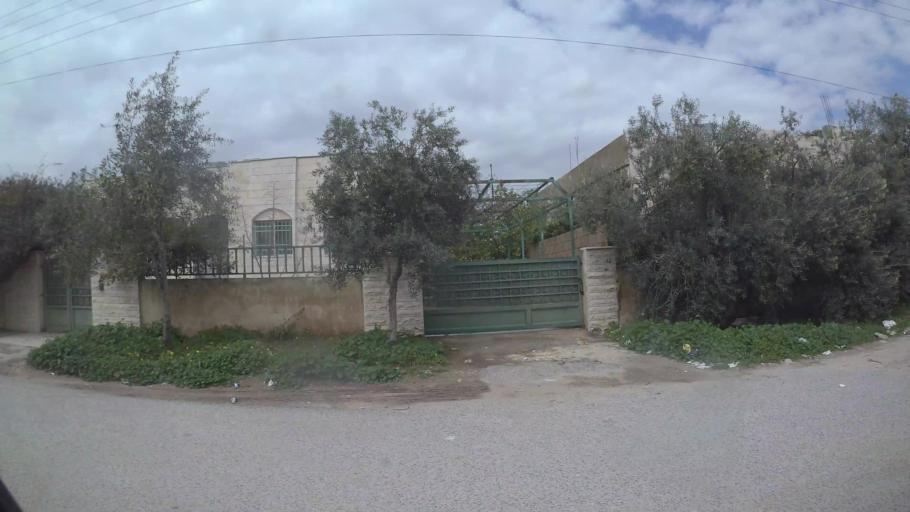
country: JO
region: Amman
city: Al Jubayhah
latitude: 32.0558
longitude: 35.8257
